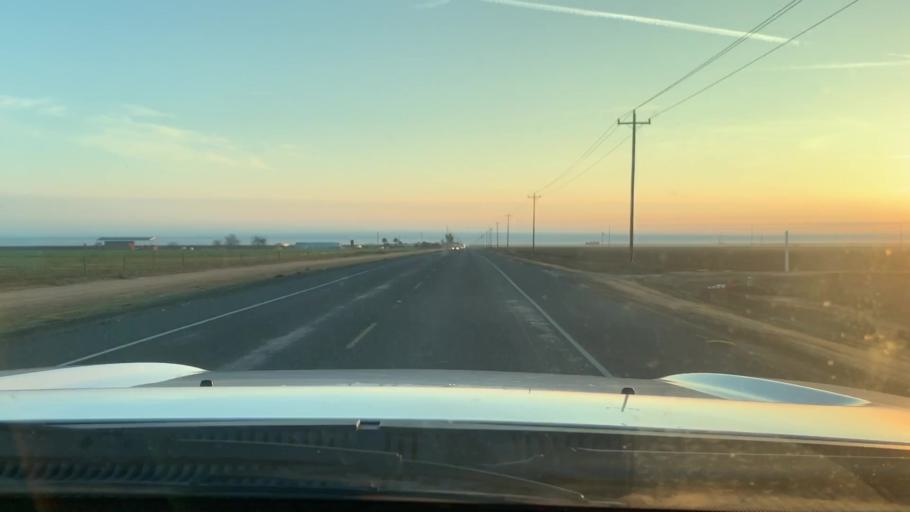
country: US
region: California
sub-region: Kern County
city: Lost Hills
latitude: 35.6011
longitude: -119.5514
